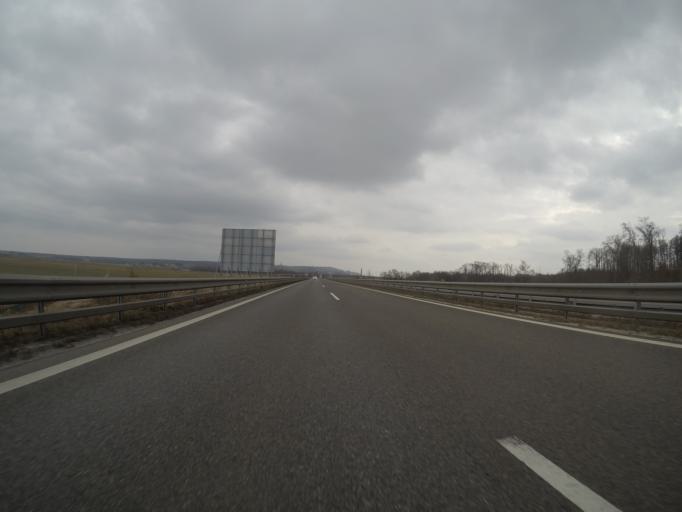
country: SI
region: Lendava-Lendva
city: Lendava
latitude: 46.5902
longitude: 16.4247
